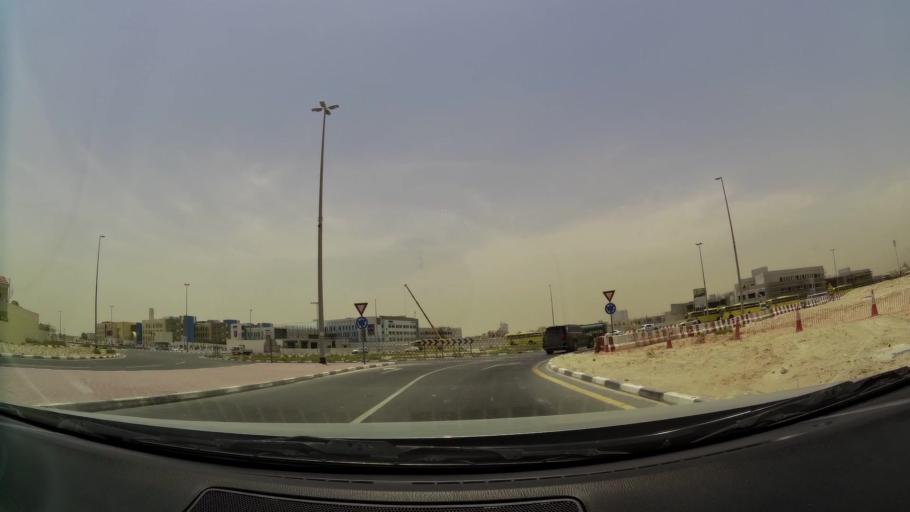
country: AE
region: Dubai
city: Dubai
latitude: 25.0809
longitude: 55.2263
